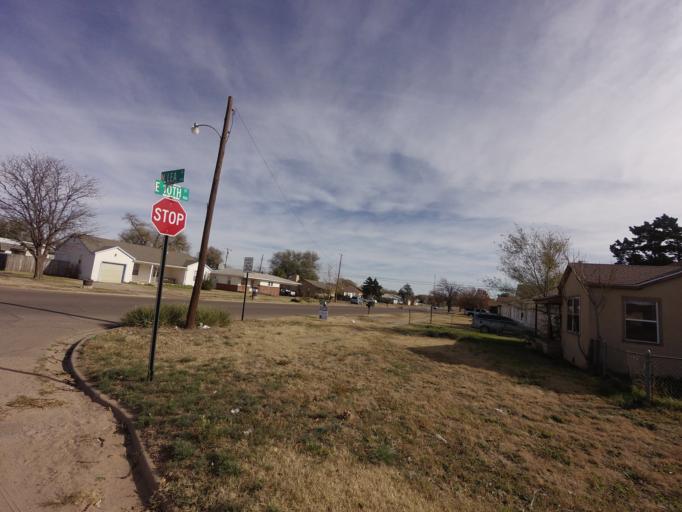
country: US
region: New Mexico
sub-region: Curry County
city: Clovis
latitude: 34.4077
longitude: -103.1952
